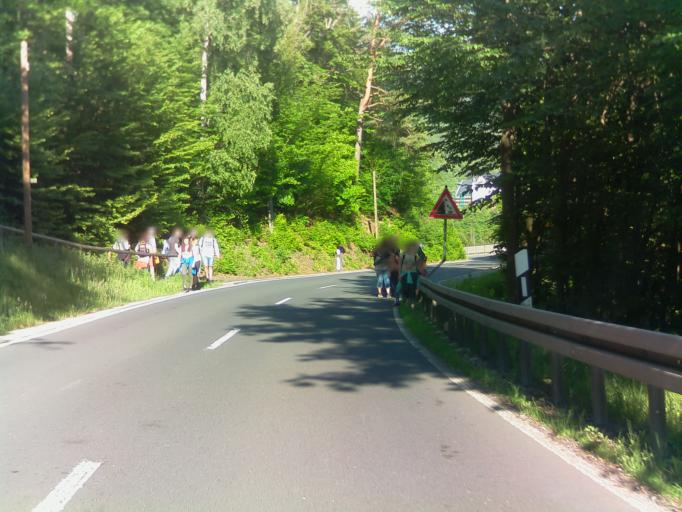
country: DE
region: Thuringia
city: Schwarzburg
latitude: 50.6422
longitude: 11.1843
